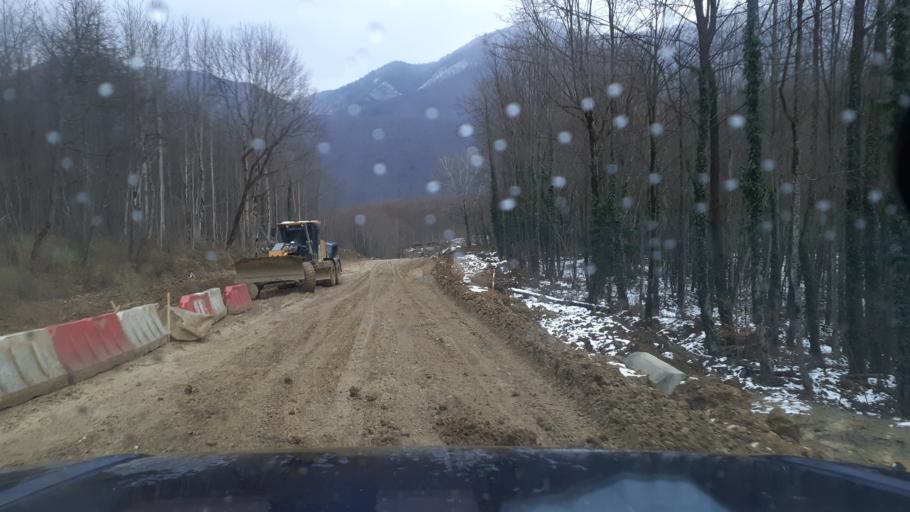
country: RU
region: Krasnodarskiy
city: Neftegorsk
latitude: 44.1638
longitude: 39.8182
